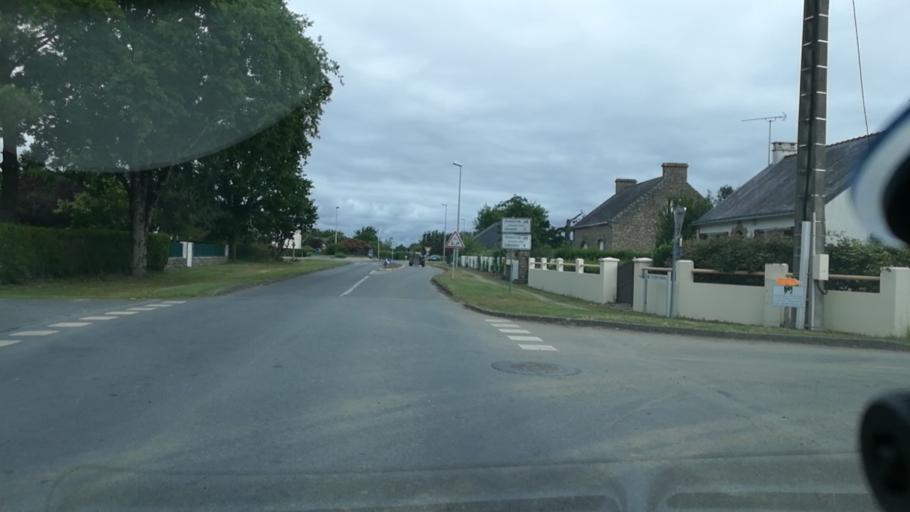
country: FR
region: Brittany
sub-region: Departement du Morbihan
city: Penestin
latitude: 47.4758
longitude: -2.4791
